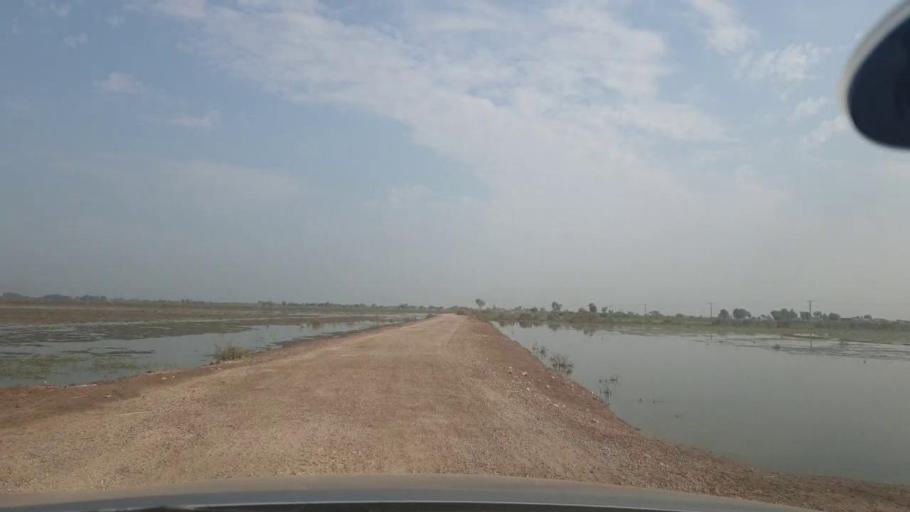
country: PK
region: Balochistan
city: Mehrabpur
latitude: 28.0635
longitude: 68.2100
